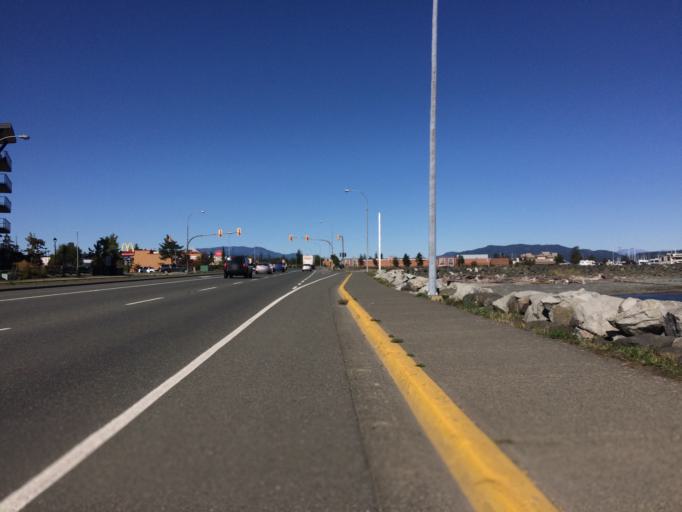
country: CA
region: British Columbia
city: Campbell River
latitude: 50.0294
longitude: -125.2441
